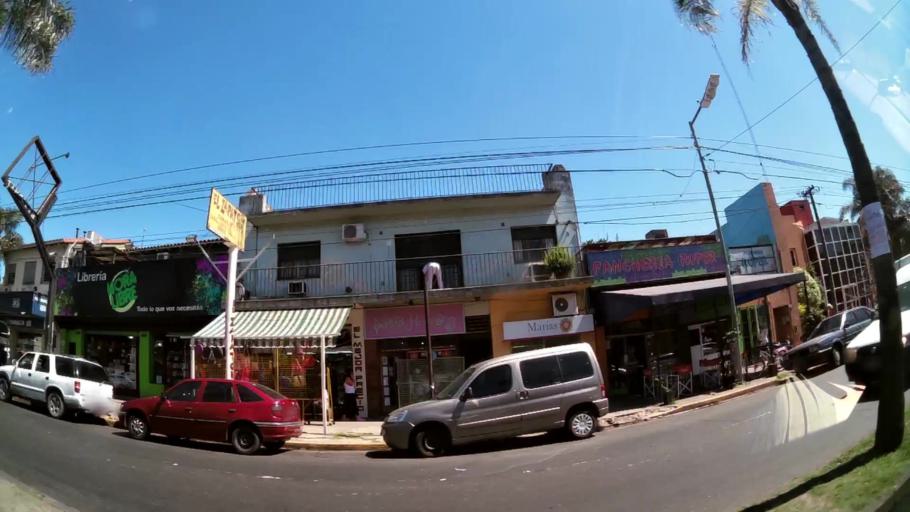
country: AR
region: Buenos Aires
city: Hurlingham
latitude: -34.4991
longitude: -58.6408
